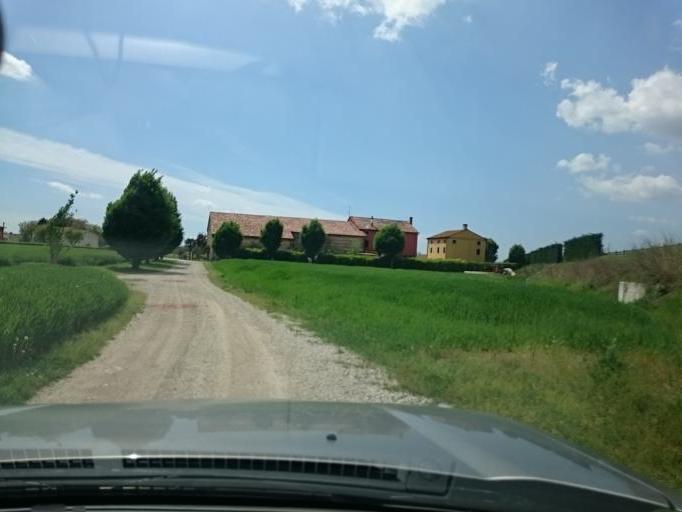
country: IT
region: Veneto
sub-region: Provincia di Vicenza
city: Villaganzerla
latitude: 45.4553
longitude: 11.6379
